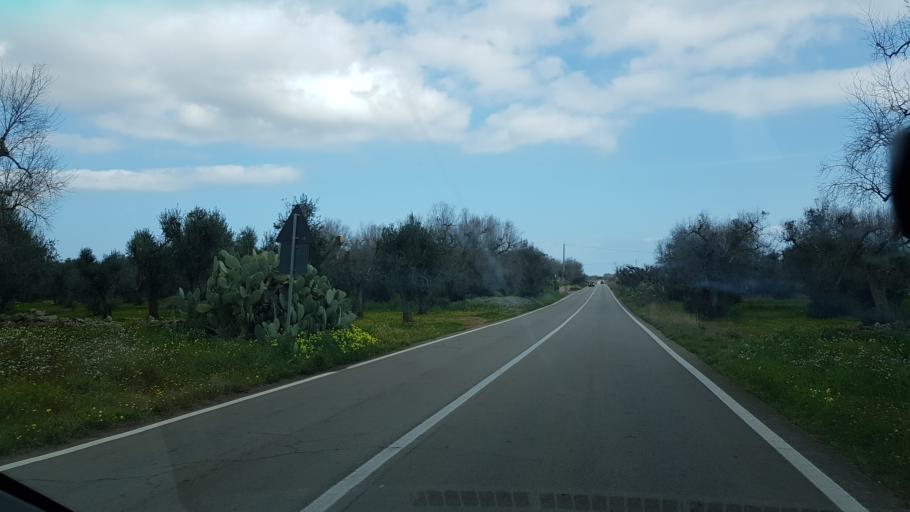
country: IT
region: Apulia
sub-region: Provincia di Brindisi
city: Torchiarolo
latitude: 40.4625
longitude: 18.0724
